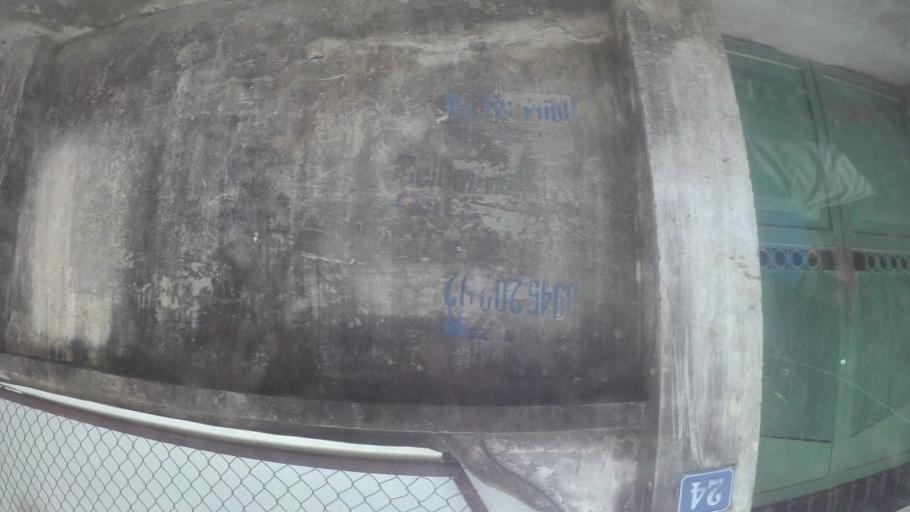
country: VN
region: Ha Noi
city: Tay Ho
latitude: 21.0862
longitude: 105.8020
